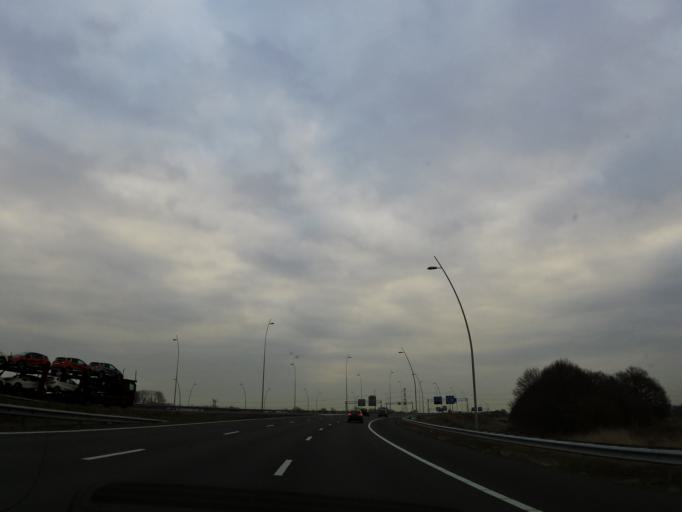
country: NL
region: North Brabant
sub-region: Gemeente Best
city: Best
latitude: 51.4826
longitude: 5.4060
